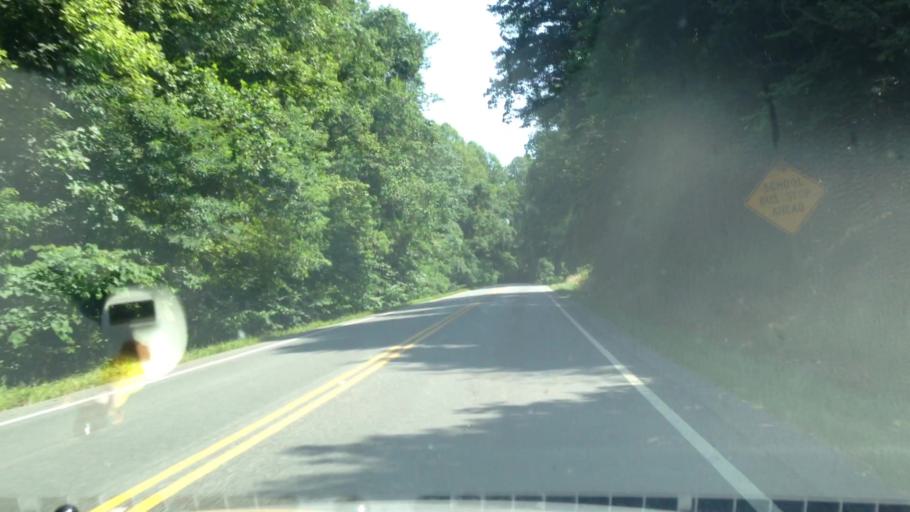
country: US
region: Virginia
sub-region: Patrick County
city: Stuart
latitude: 36.5874
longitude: -80.3309
